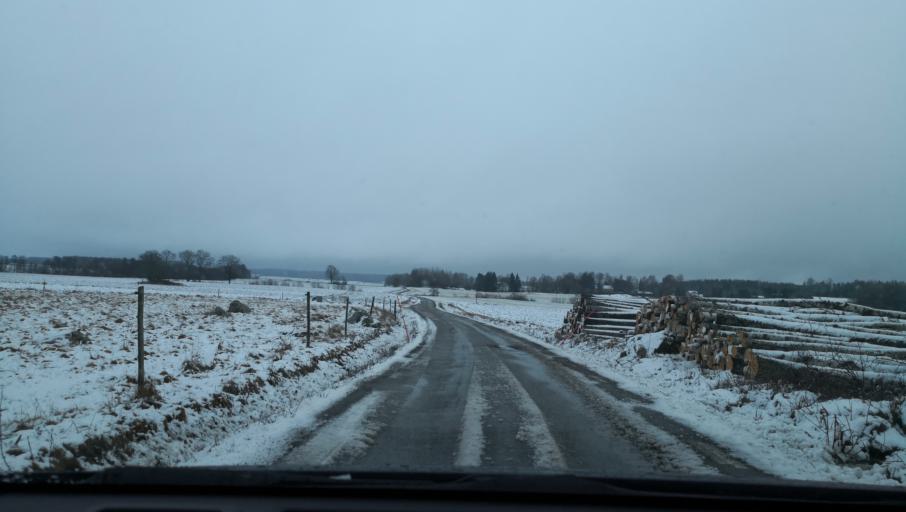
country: SE
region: Vaestmanland
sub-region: Kopings Kommun
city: Kolsva
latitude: 59.5420
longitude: 15.8816
